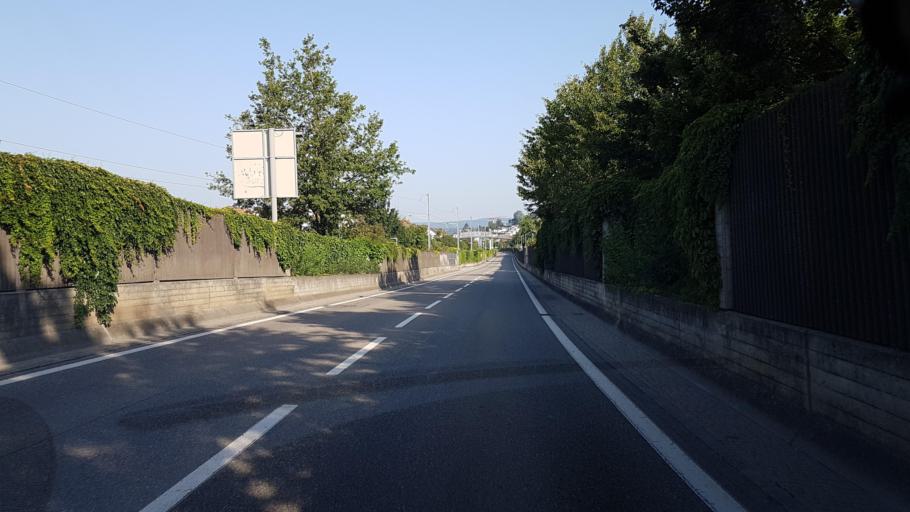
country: CH
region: Aargau
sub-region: Bezirk Zurzach
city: Klingnau
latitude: 47.5784
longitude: 8.2555
